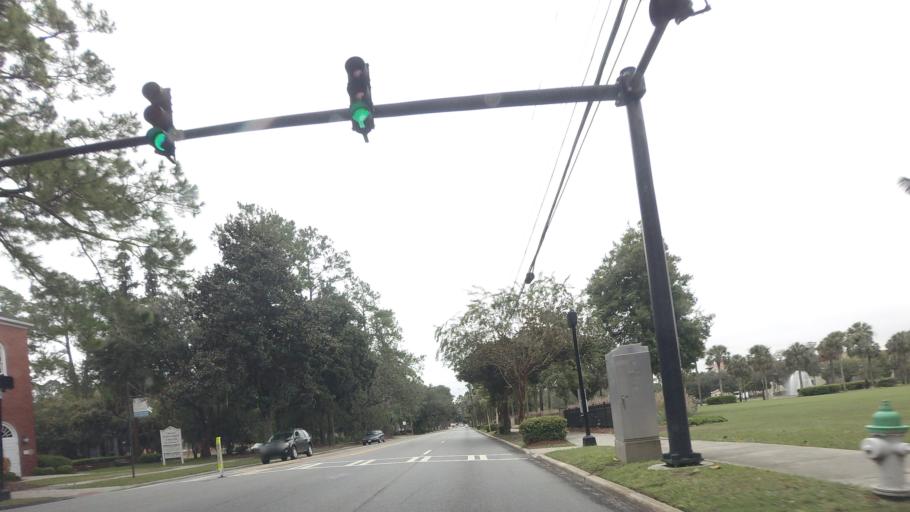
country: US
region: Georgia
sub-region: Lowndes County
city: Valdosta
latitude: 30.8504
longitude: -83.2878
